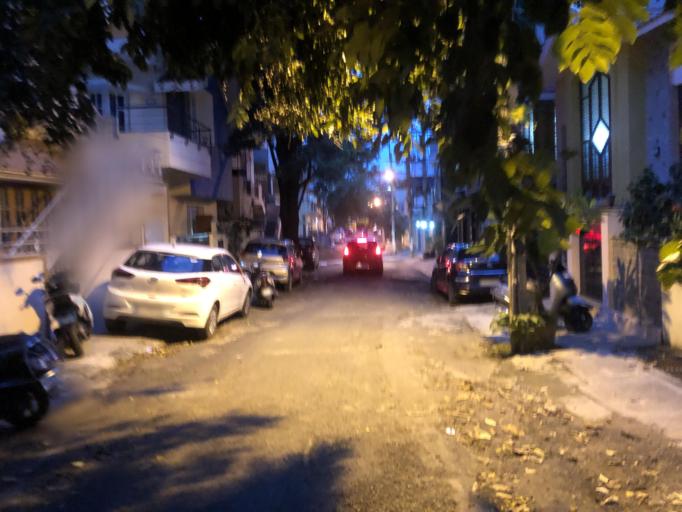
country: IN
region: Karnataka
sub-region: Bangalore Urban
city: Bangalore
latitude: 12.9365
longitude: 77.5461
